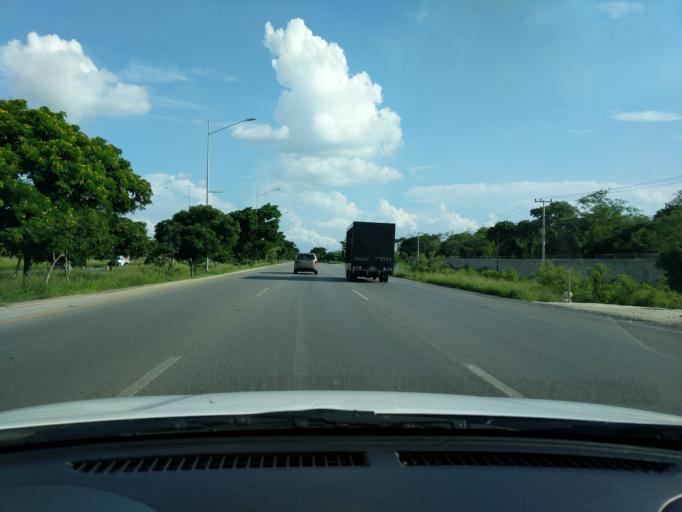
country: MX
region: Yucatan
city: Itzincab Palomeque
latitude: 20.9365
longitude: -89.6953
